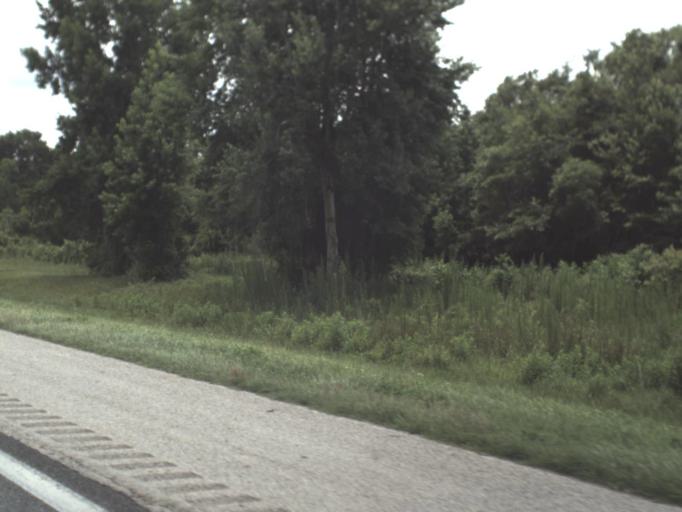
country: US
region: Florida
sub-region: Alachua County
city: Gainesville
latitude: 29.5416
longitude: -82.3310
